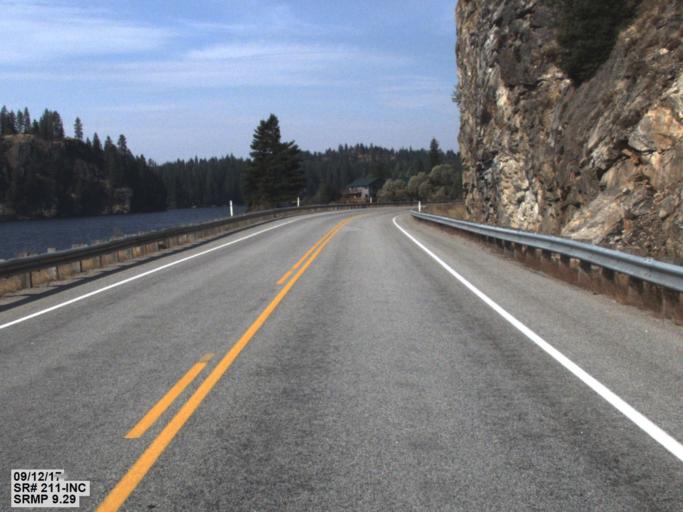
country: US
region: Washington
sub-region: Pend Oreille County
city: Newport
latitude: 48.2216
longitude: -117.2916
